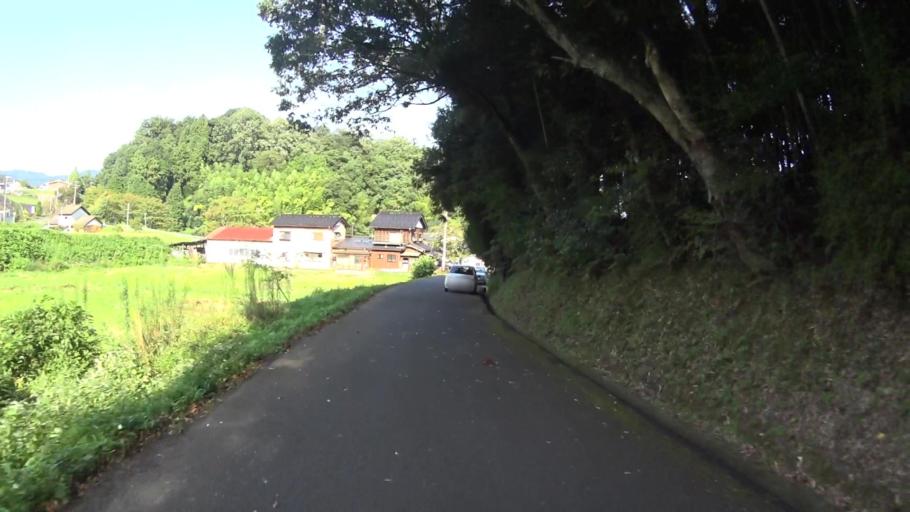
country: JP
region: Kyoto
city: Miyazu
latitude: 35.5635
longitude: 135.1440
